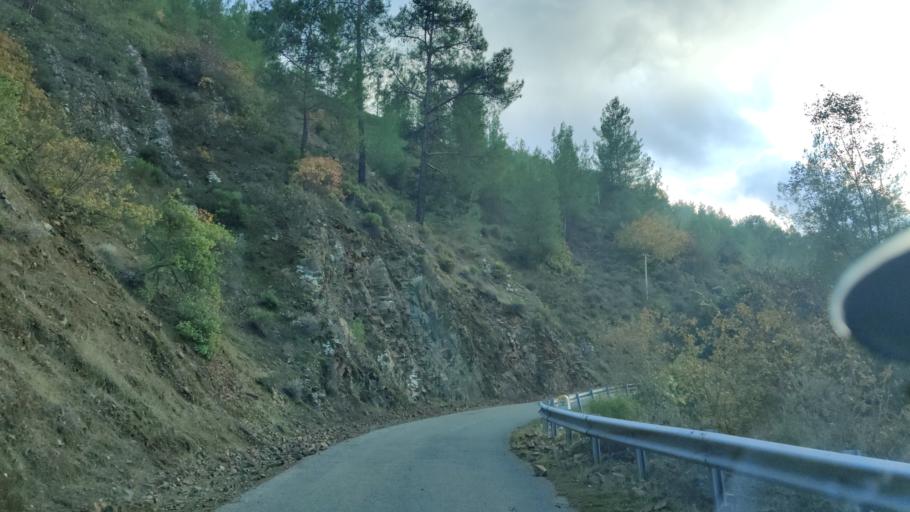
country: CY
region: Lefkosia
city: Lefka
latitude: 35.0706
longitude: 32.7423
